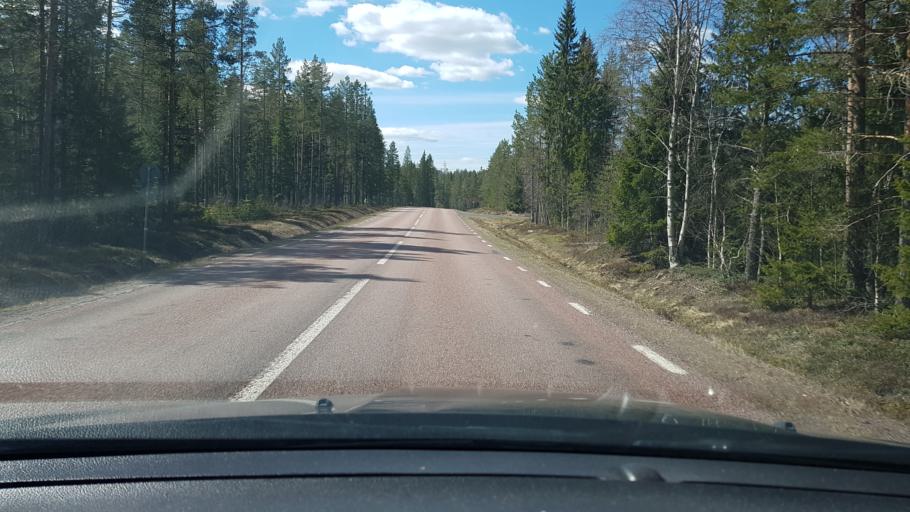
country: SE
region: Dalarna
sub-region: Malung-Saelens kommun
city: Malung
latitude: 61.0523
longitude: 13.4222
